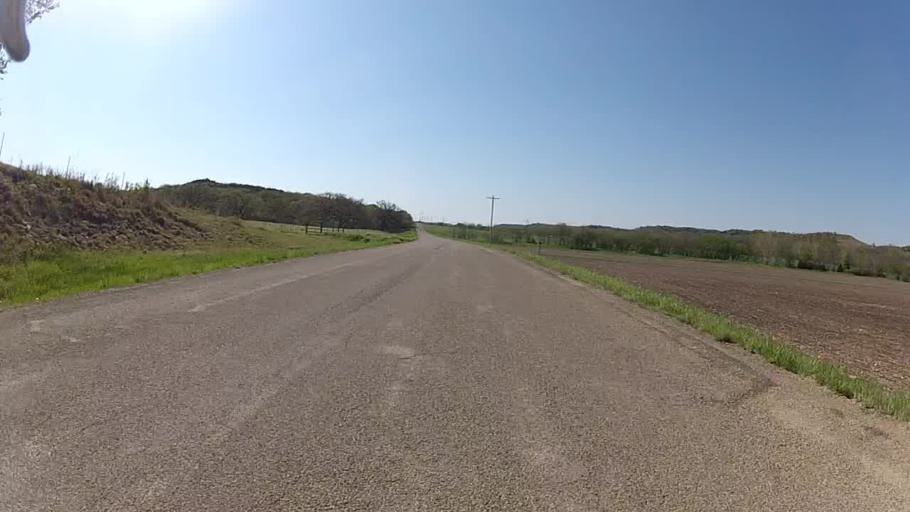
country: US
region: Kansas
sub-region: Riley County
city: Ogden
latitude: 39.0270
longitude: -96.6997
